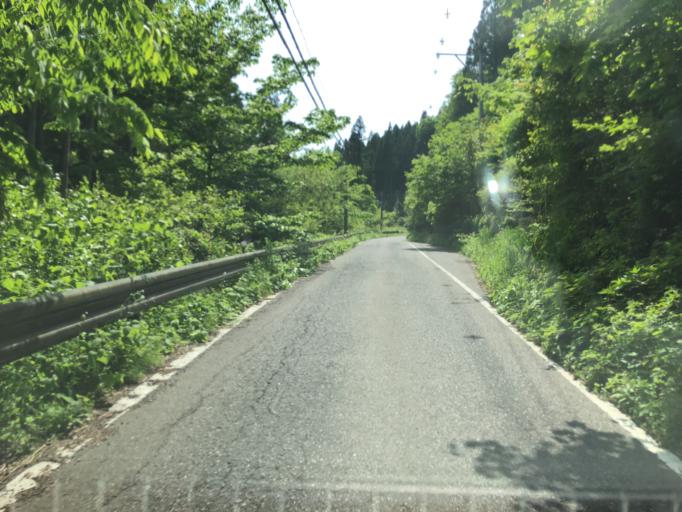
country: JP
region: Fukushima
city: Ishikawa
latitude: 37.0485
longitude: 140.5764
